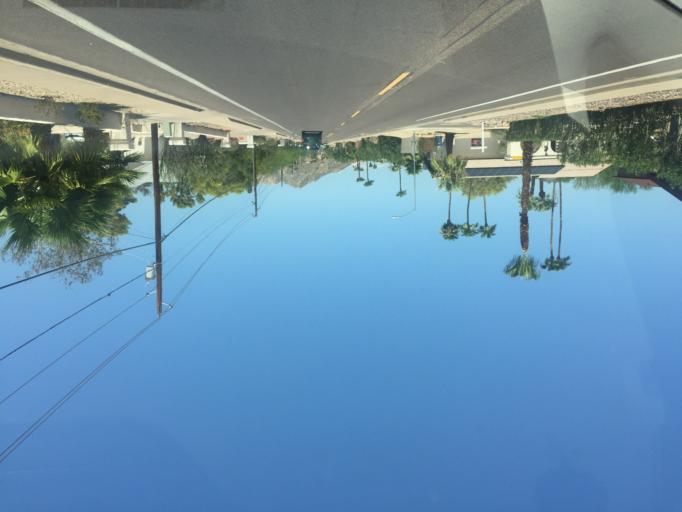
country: US
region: Arizona
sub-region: Maricopa County
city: Paradise Valley
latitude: 33.5899
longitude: -112.0305
